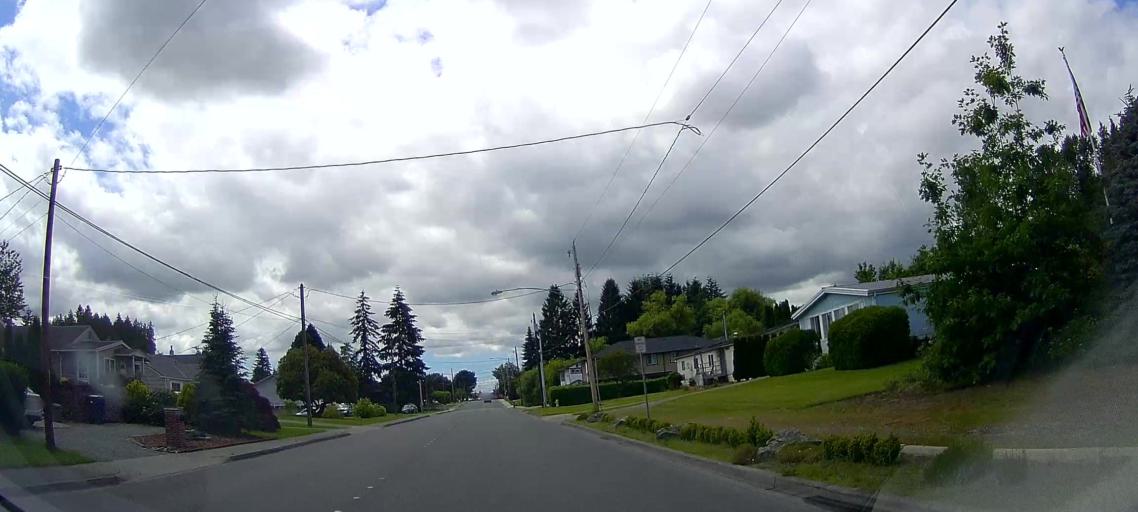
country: US
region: Washington
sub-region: Skagit County
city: Burlington
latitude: 48.4755
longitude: -122.3159
